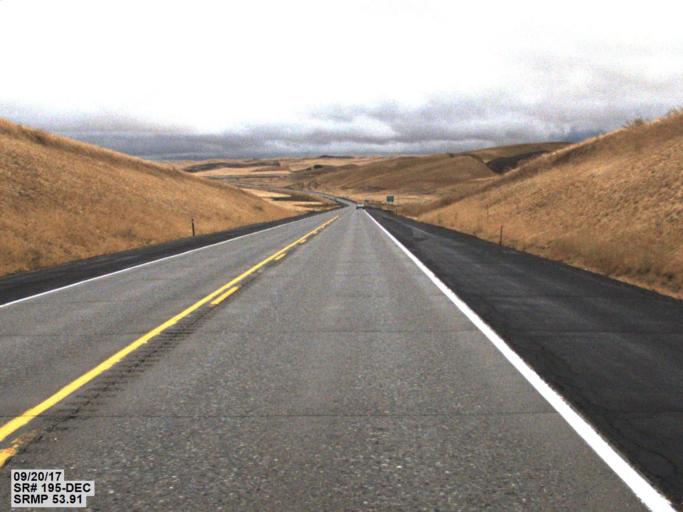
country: US
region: Washington
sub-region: Whitman County
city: Colfax
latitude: 47.0870
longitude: -117.3809
